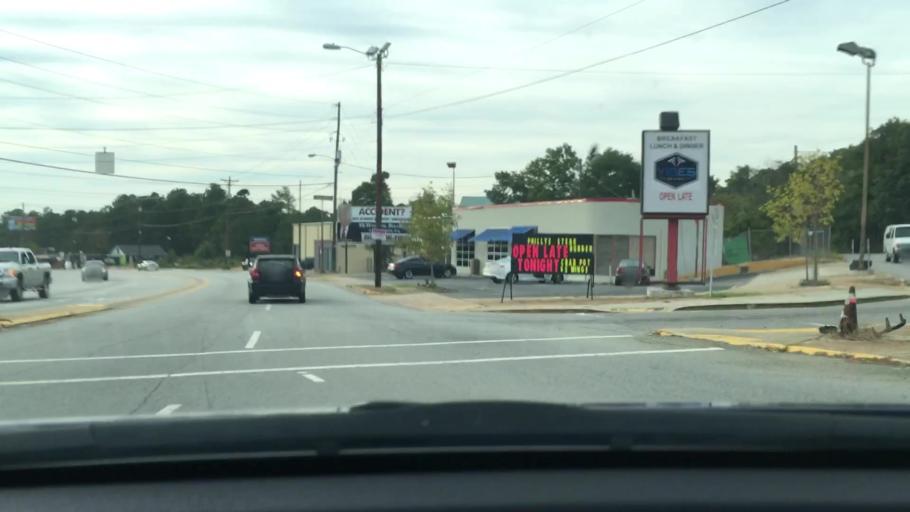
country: US
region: South Carolina
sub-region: Richland County
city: Columbia
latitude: 34.0293
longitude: -81.0560
